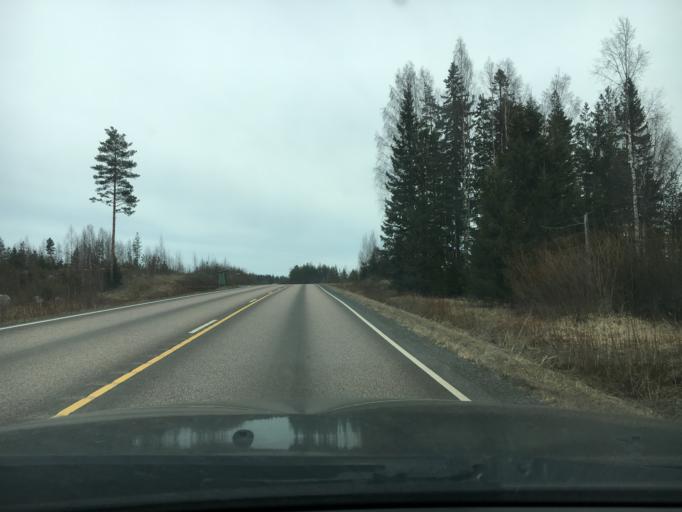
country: FI
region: Central Finland
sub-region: AEaenekoski
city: Konnevesi
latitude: 62.6746
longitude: 26.3572
